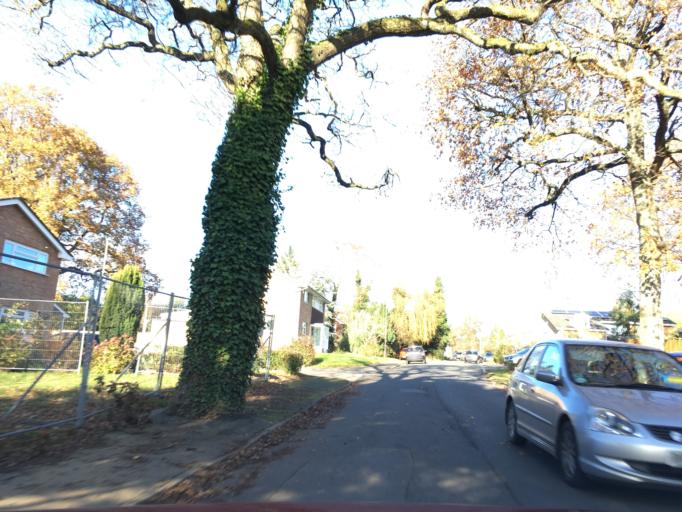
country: GB
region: England
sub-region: Hampshire
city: Colden Common
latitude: 50.9917
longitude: -1.3185
